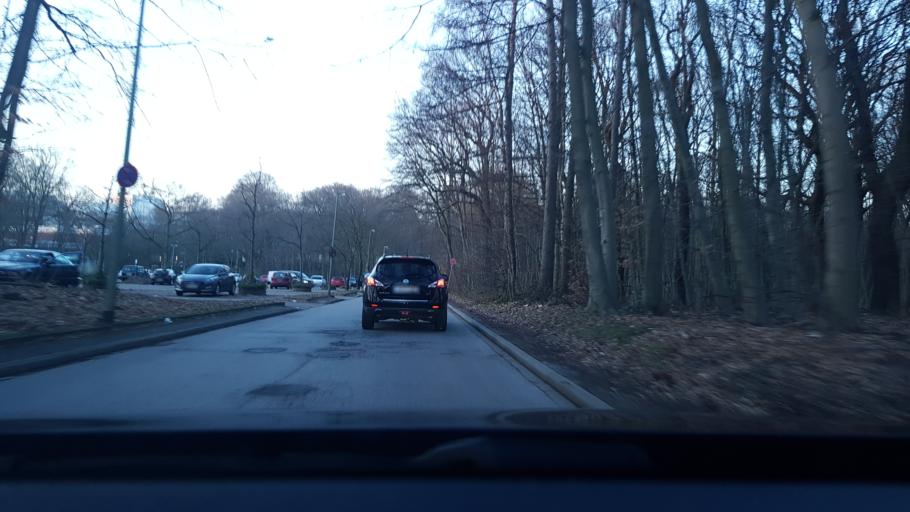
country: DE
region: North Rhine-Westphalia
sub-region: Regierungsbezirk Dusseldorf
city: Duisburg
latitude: 51.4295
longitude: 6.8029
